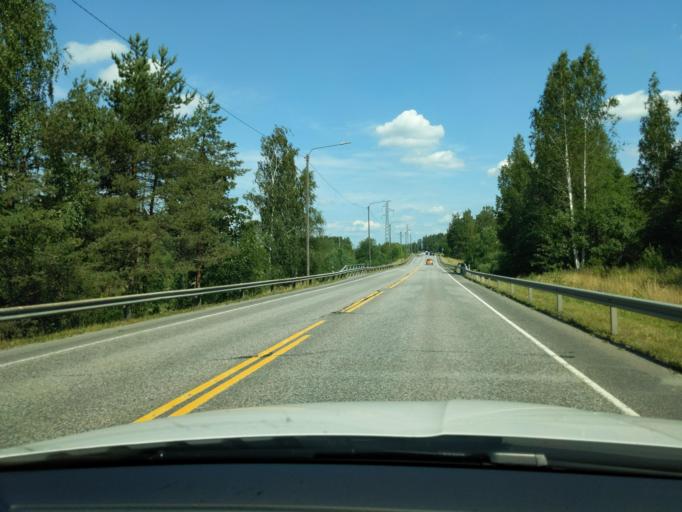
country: FI
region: Uusimaa
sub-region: Helsinki
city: Kerava
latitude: 60.3945
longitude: 25.1267
